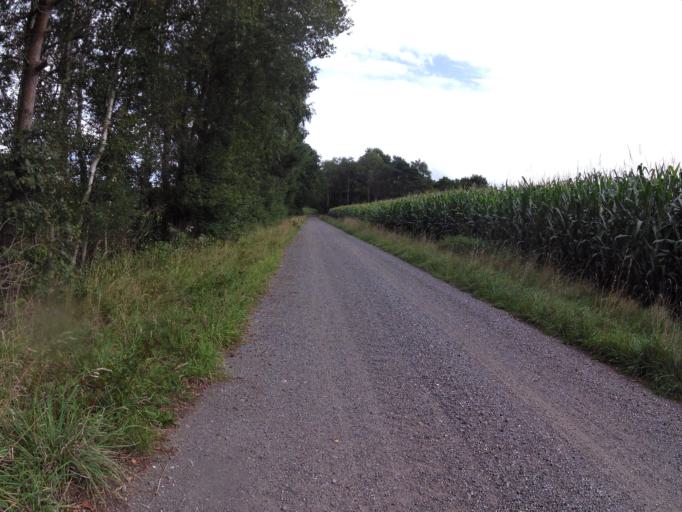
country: DE
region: Lower Saxony
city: Hipstedt
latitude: 53.5013
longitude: 8.9205
